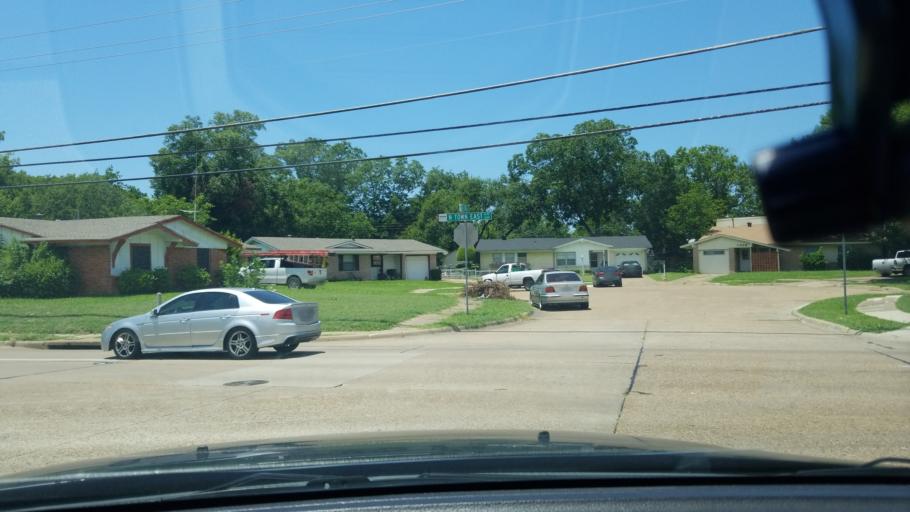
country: US
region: Texas
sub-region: Dallas County
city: Mesquite
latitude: 32.7982
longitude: -96.6505
